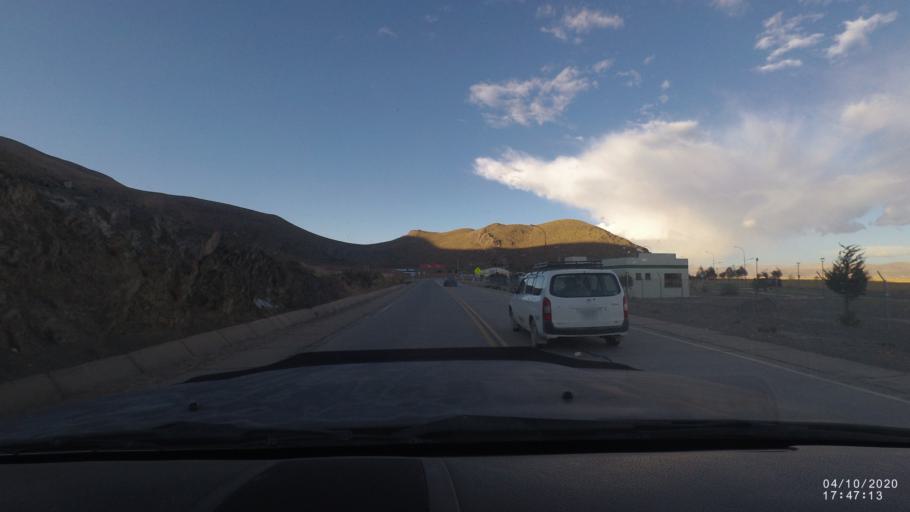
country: BO
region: Oruro
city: Oruro
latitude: -18.0250
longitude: -67.1452
